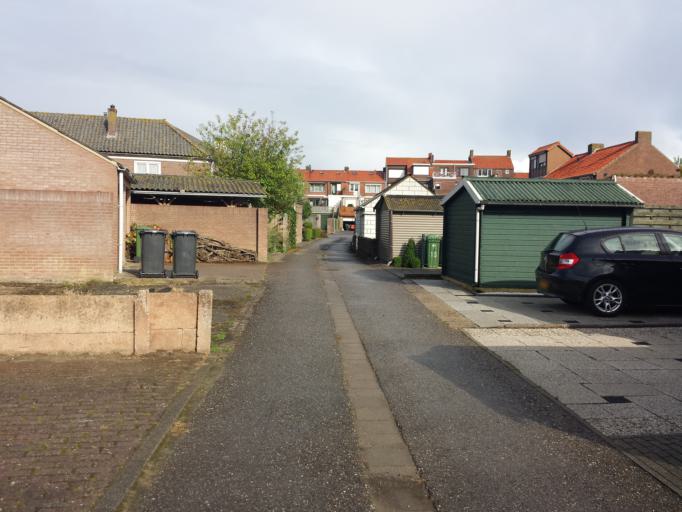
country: NL
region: Zeeland
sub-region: Gemeente Vlissingen
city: Vlissingen
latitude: 51.3939
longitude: 3.5629
